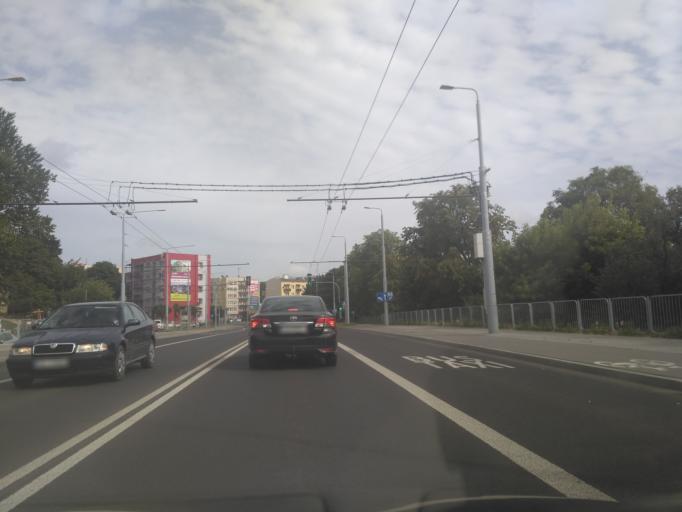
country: PL
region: Lublin Voivodeship
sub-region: Powiat lubelski
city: Lublin
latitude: 51.2367
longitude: 22.5556
